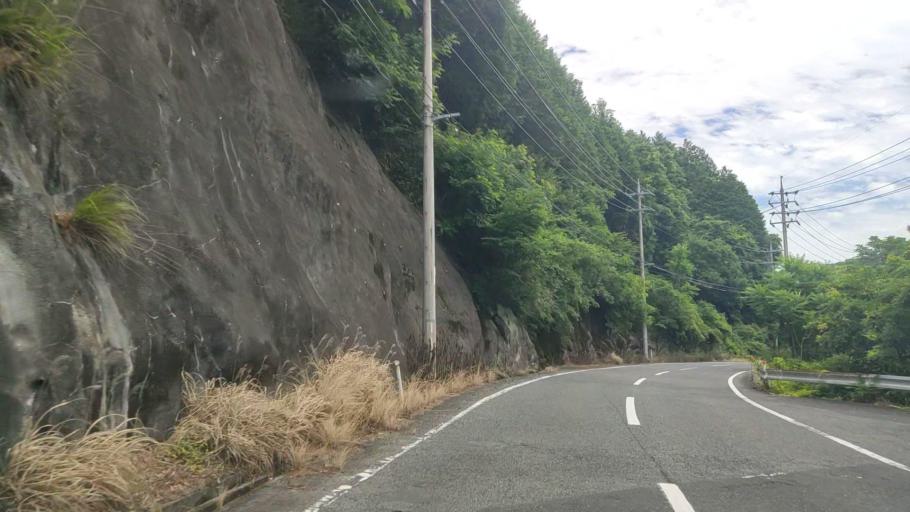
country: JP
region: Okayama
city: Tsuyama
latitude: 35.0667
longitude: 134.2272
